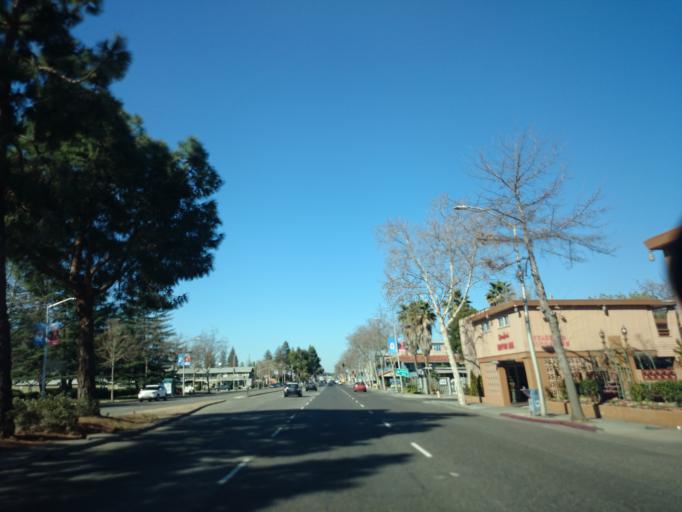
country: US
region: California
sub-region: Santa Clara County
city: Palo Alto
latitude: 37.4203
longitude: -122.1366
